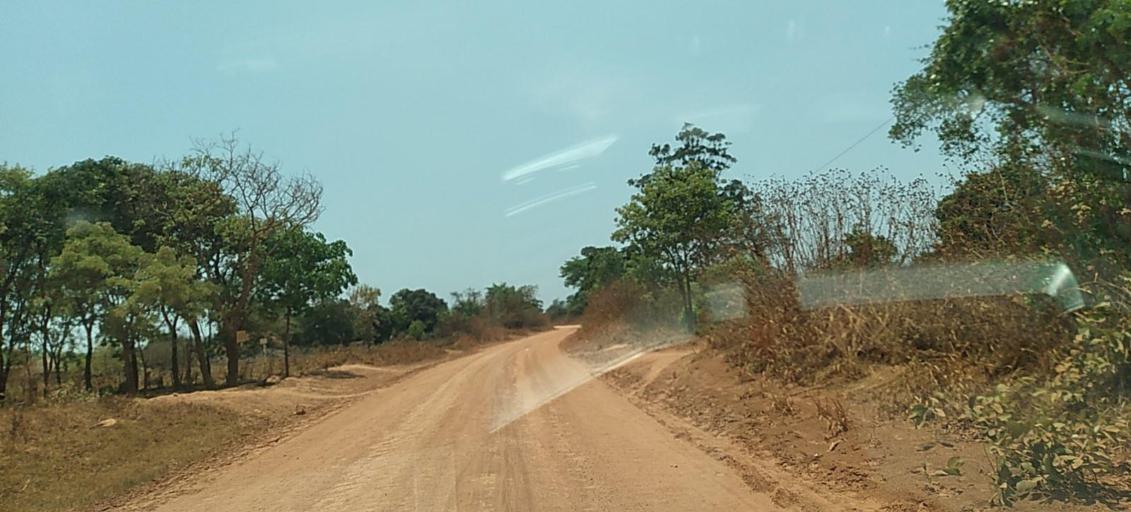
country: CD
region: Katanga
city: Kipushi
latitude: -11.7829
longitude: 27.1791
